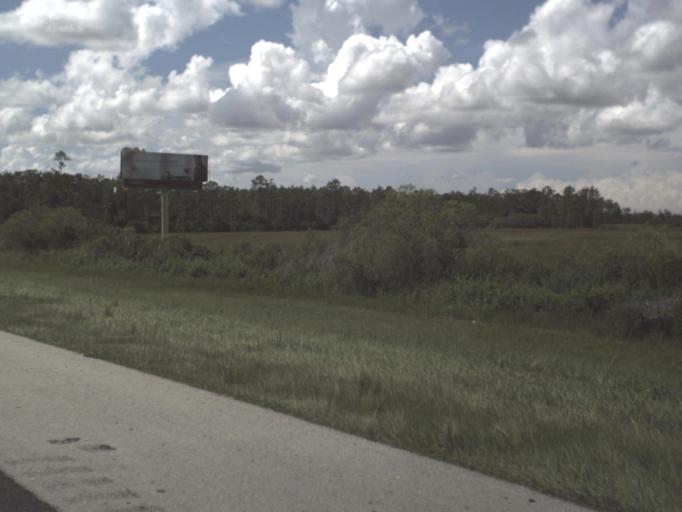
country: US
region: Florida
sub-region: Lee County
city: Fort Myers
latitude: 26.6060
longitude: -81.8014
